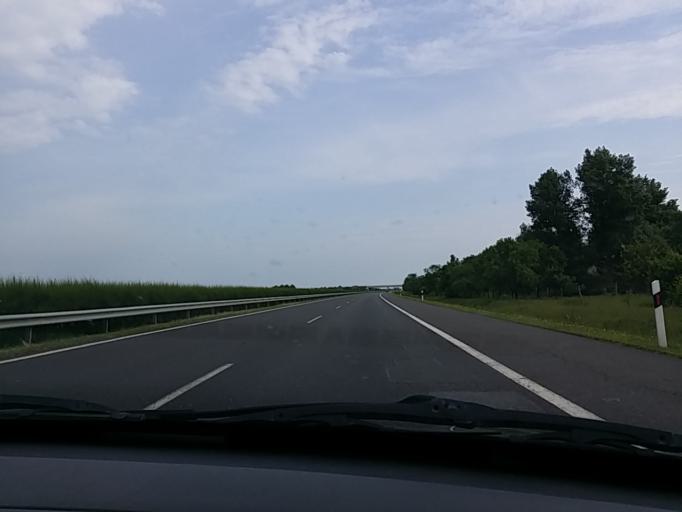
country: HU
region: Borsod-Abauj-Zemplen
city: Emod
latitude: 47.8988
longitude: 20.8361
